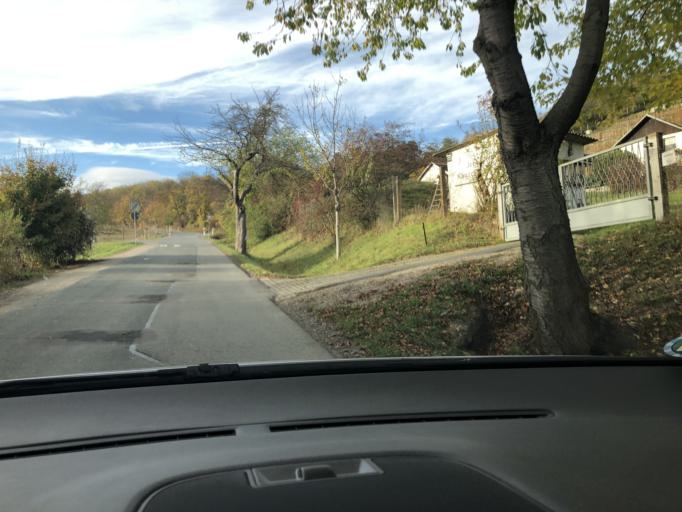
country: DE
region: Thuringia
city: Lehesten
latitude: 50.9616
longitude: 11.6091
